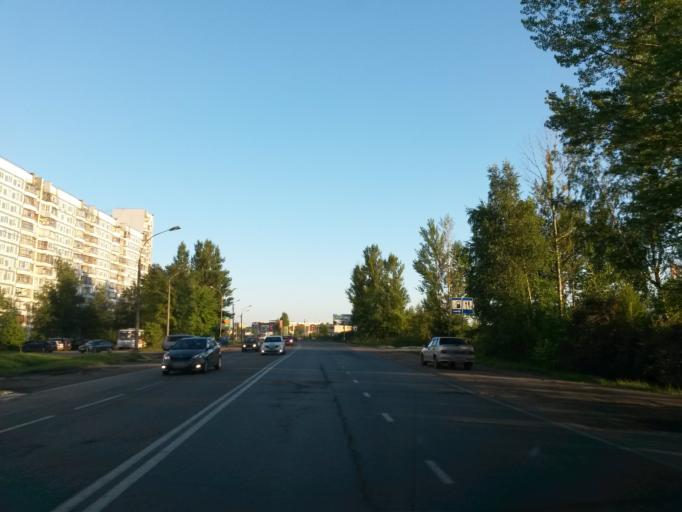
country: RU
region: Jaroslavl
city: Yaroslavl
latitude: 57.7048
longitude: 39.7591
